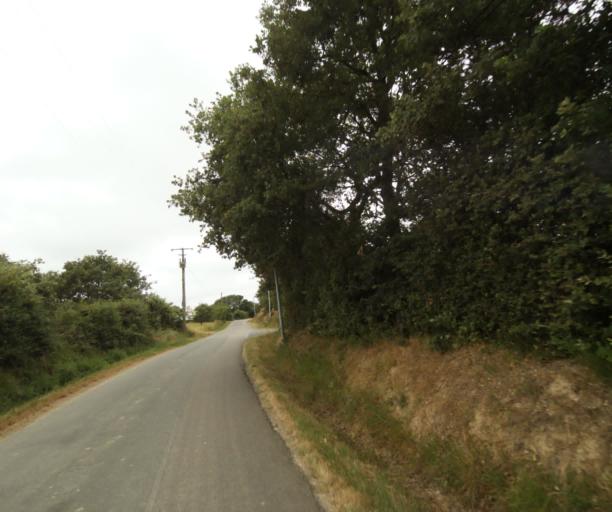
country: FR
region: Pays de la Loire
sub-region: Departement de la Vendee
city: Chateau-d'Olonne
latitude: 46.4982
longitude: -1.7134
